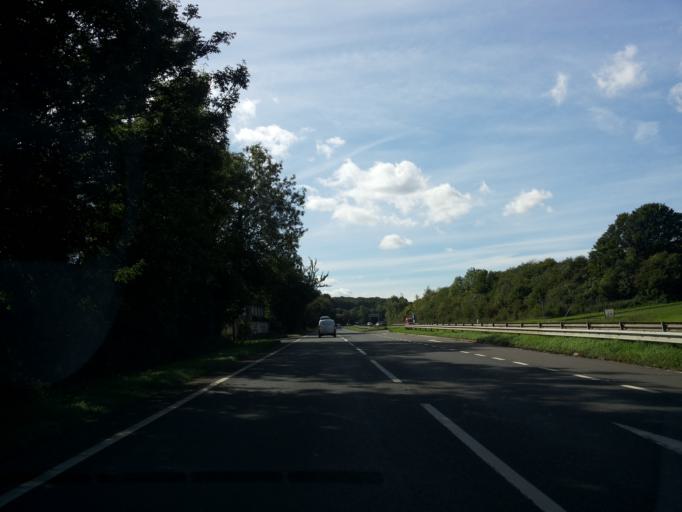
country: GB
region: England
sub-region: Kent
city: Newington
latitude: 51.3201
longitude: 0.6492
